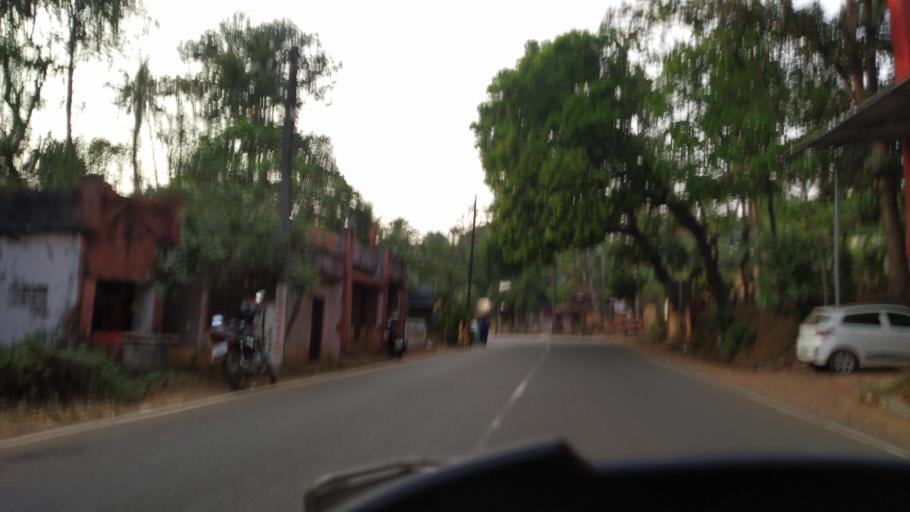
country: IN
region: Kerala
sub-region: Kottayam
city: Lalam
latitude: 9.5661
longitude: 76.7050
